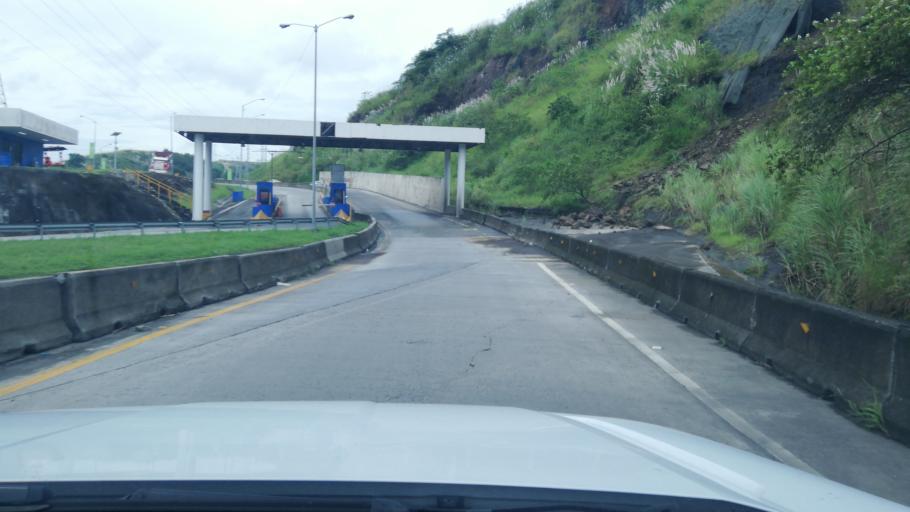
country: PA
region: Panama
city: Las Cumbres
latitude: 9.0602
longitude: -79.5103
